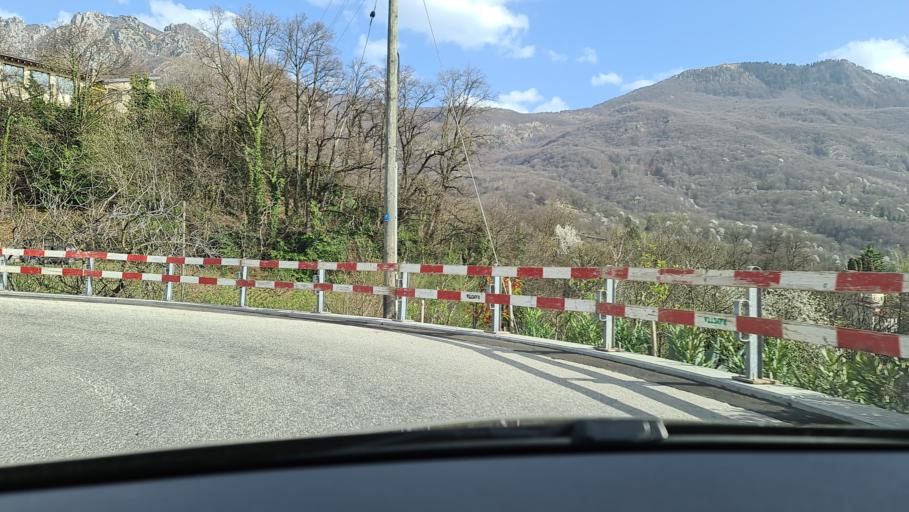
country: CH
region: Ticino
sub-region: Lugano District
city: Cadro
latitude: 46.0530
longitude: 8.9863
